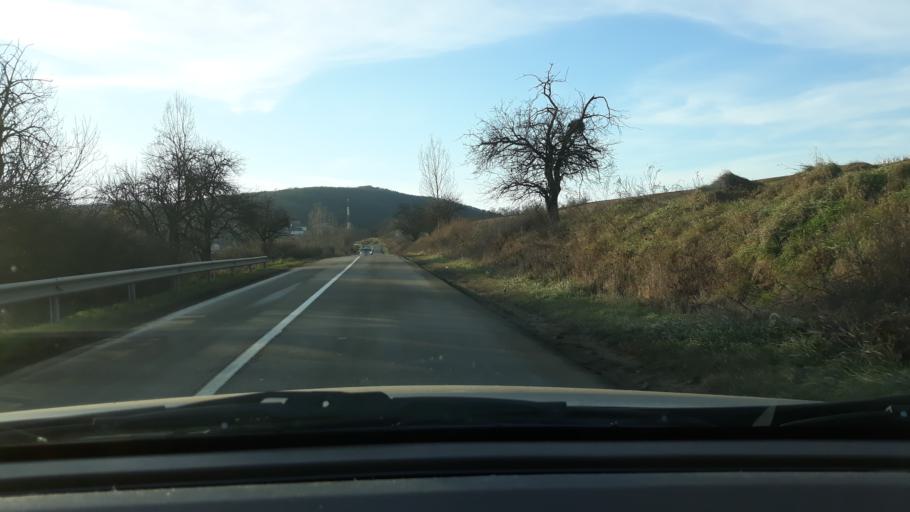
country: RO
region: Salaj
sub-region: Comuna Marca
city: Marca
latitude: 47.2273
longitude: 22.5608
